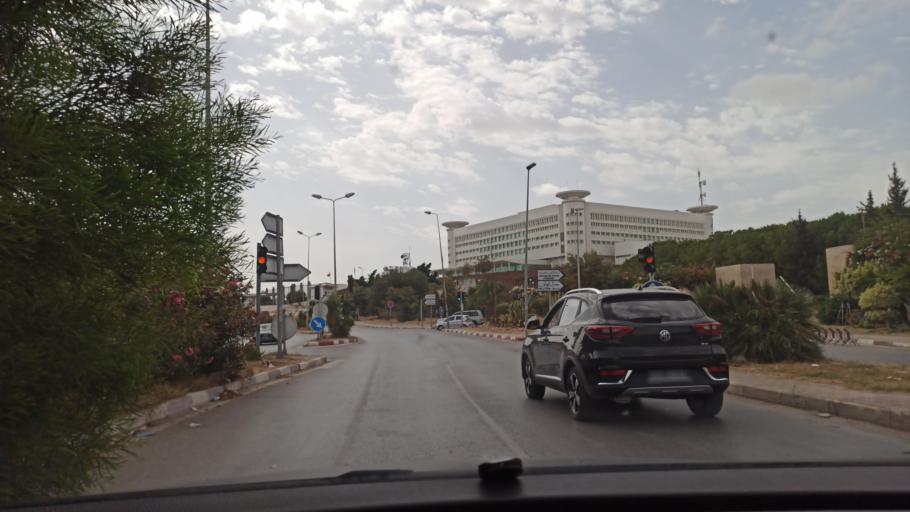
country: TN
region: Tunis
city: Tunis
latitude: 36.8311
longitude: 10.1576
